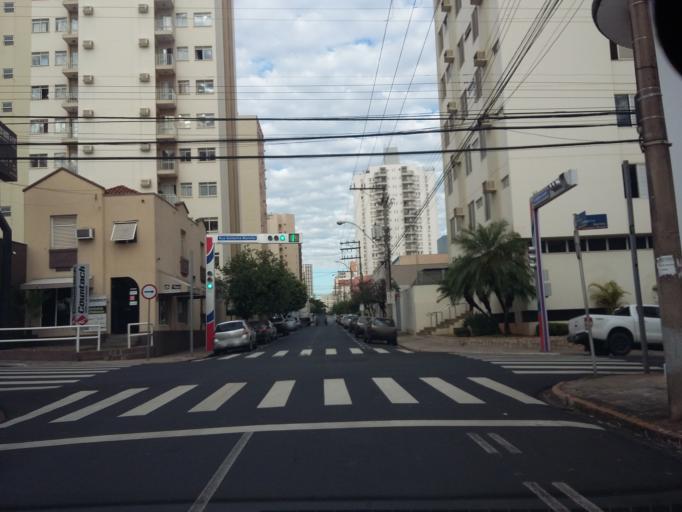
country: BR
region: Sao Paulo
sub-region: Sao Jose Do Rio Preto
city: Sao Jose do Rio Preto
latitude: -20.8125
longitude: -49.3862
